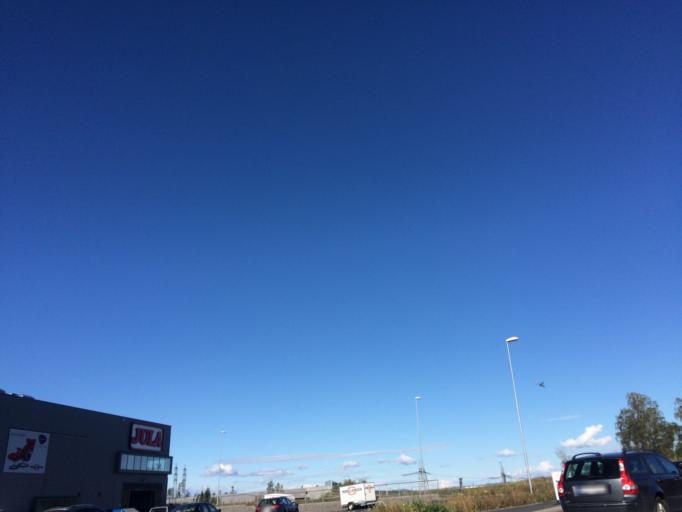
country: NO
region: Akershus
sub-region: Ski
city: Ski
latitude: 59.7254
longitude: 10.7826
